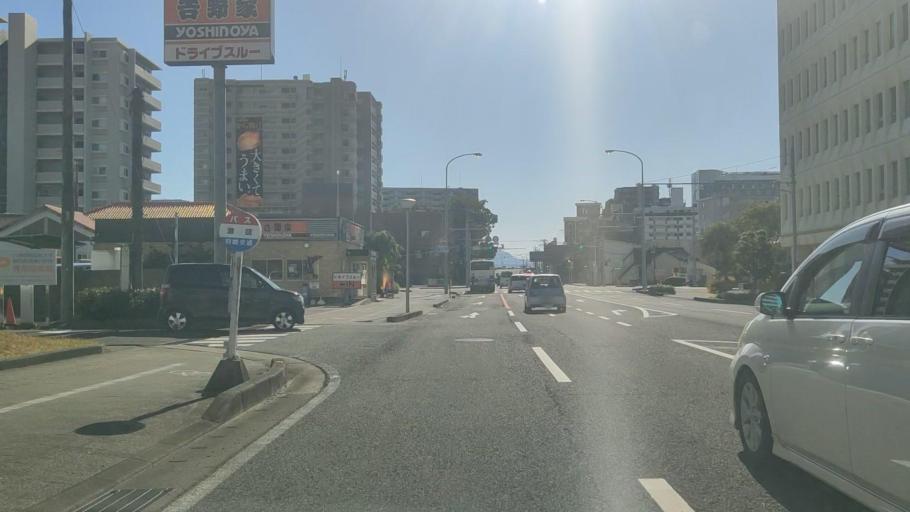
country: JP
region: Miyazaki
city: Miyazaki-shi
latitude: 31.9086
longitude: 131.4289
